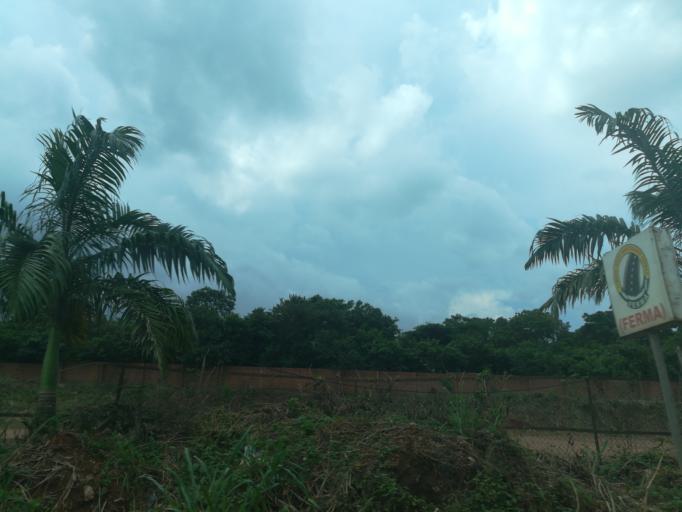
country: NG
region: Lagos
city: Ikorodu
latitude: 6.6421
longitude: 3.5520
